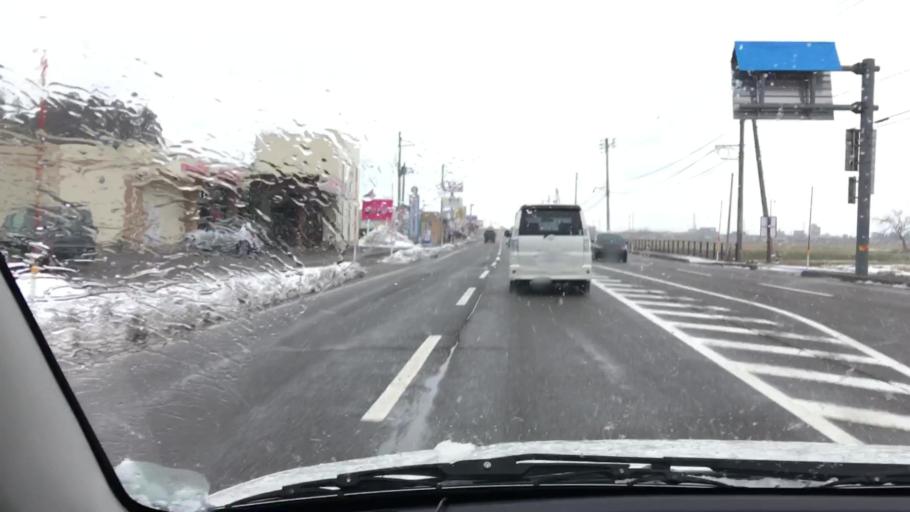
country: JP
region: Niigata
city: Joetsu
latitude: 37.1243
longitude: 138.2322
